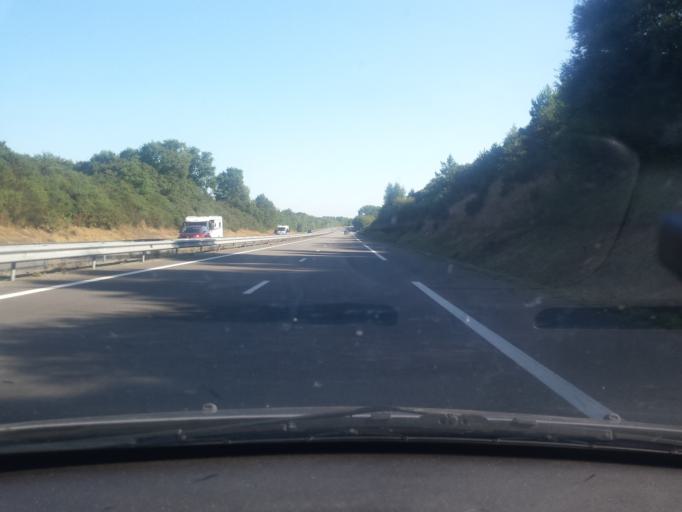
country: FR
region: Brittany
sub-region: Departement du Morbihan
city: Naizin
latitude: 47.9924
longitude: -2.8813
